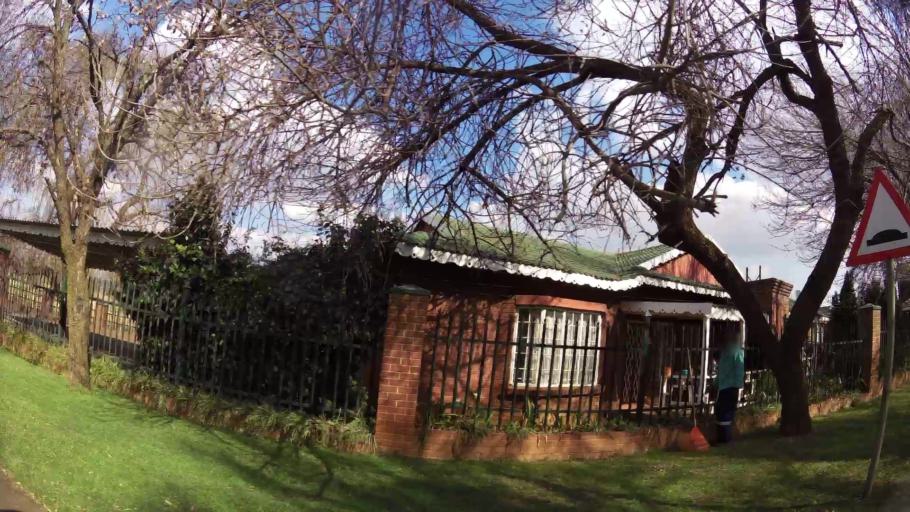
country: ZA
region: Mpumalanga
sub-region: Nkangala District Municipality
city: Delmas
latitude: -26.1424
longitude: 28.6762
